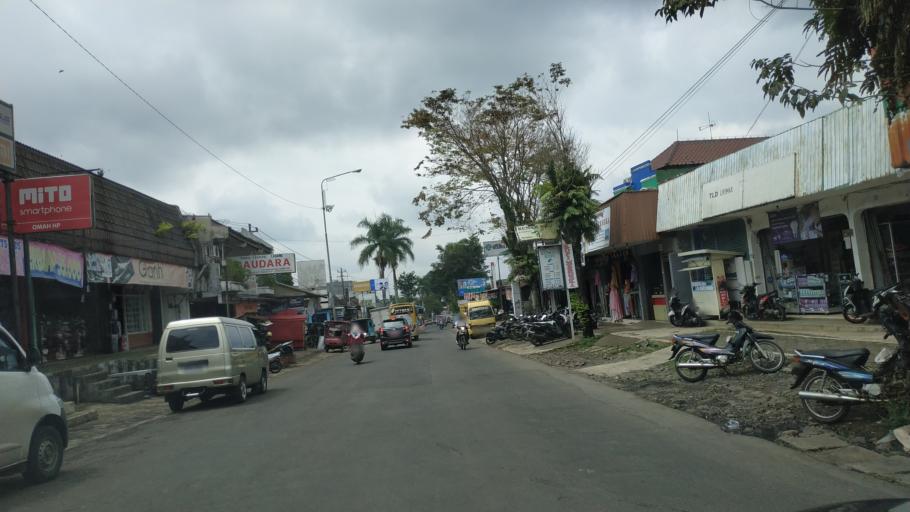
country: ID
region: Central Java
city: Weleri
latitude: -7.0877
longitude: 110.0460
